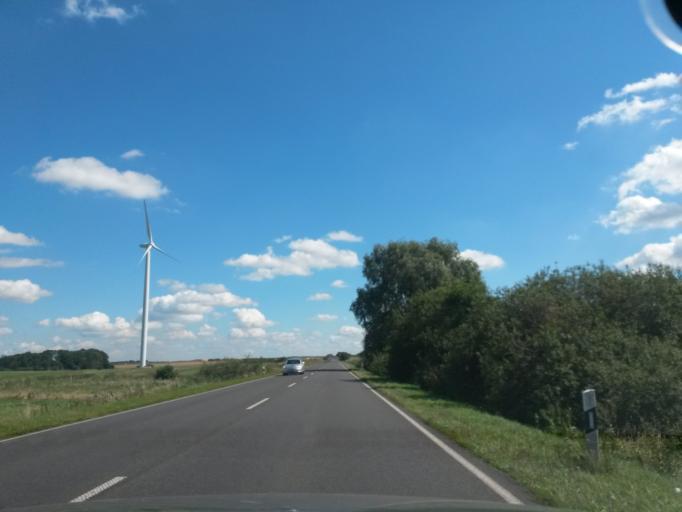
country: DE
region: Brandenburg
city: Pinnow
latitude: 53.0282
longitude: 14.0676
